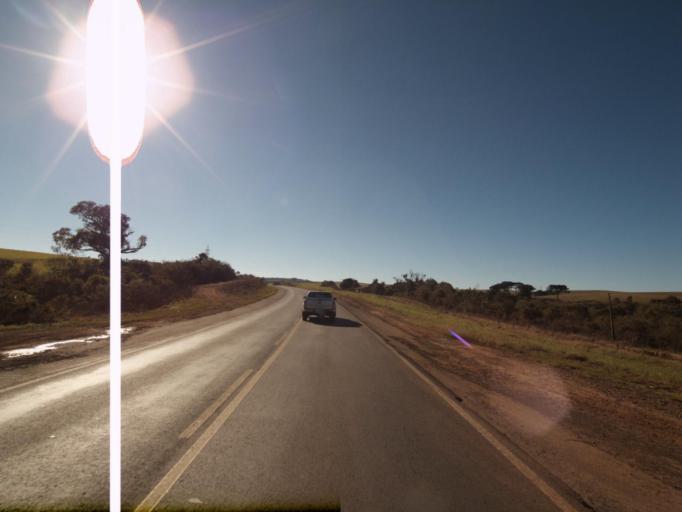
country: BR
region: Santa Catarina
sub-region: Concordia
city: Concordia
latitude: -26.9184
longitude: -51.9277
